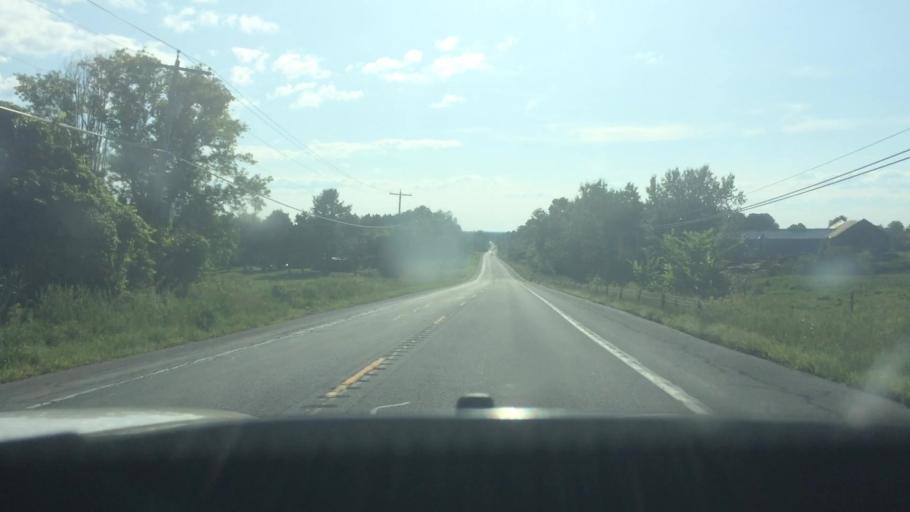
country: US
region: New York
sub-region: Franklin County
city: Malone
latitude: 44.8162
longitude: -74.3784
